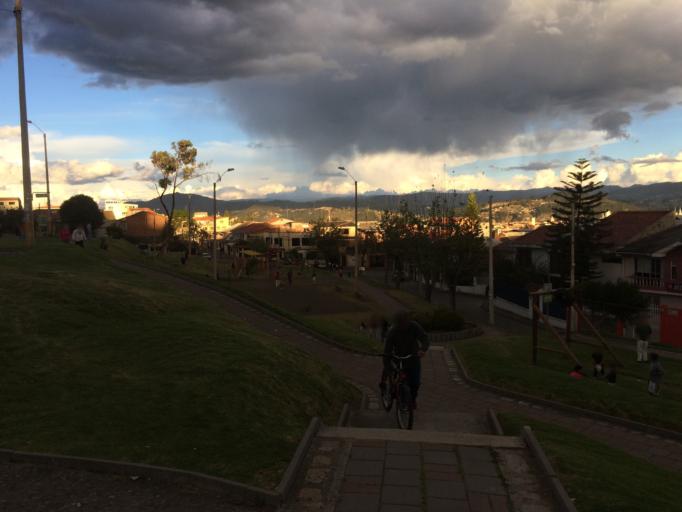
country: EC
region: Azuay
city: Cuenca
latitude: -2.8884
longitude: -79.0107
